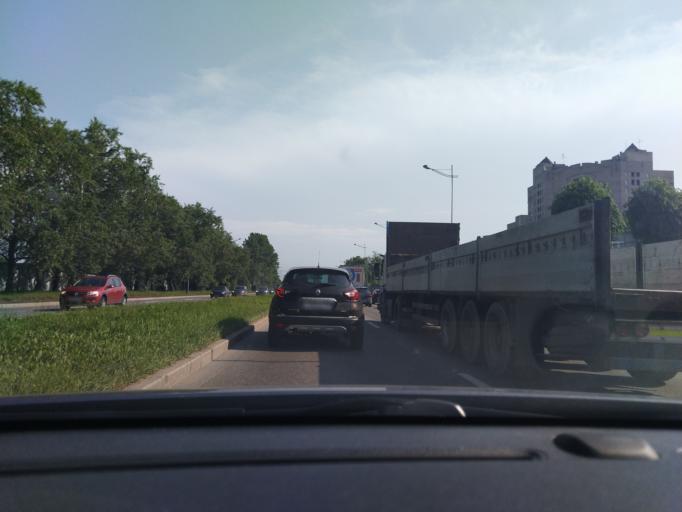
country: RU
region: St.-Petersburg
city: Kupchino
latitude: 59.8671
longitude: 30.3564
